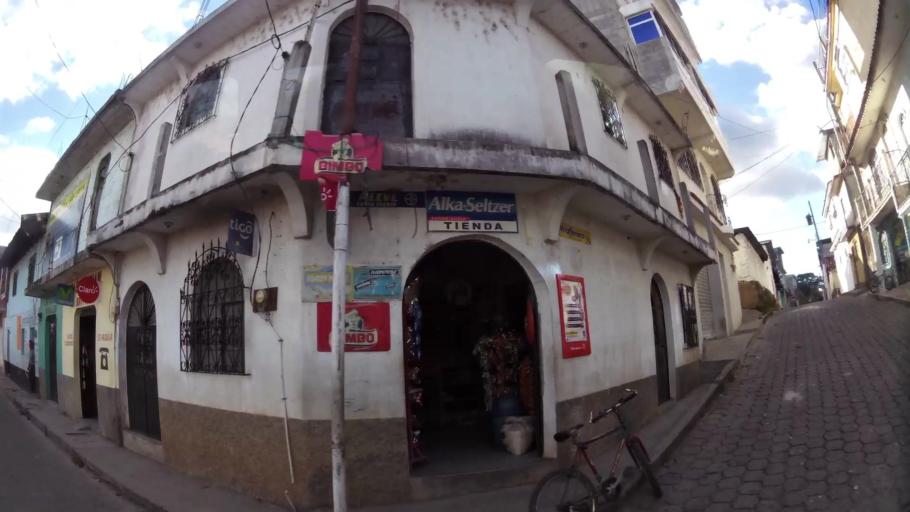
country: GT
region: Quiche
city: Chichicastenango
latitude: 14.9465
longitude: -91.1113
